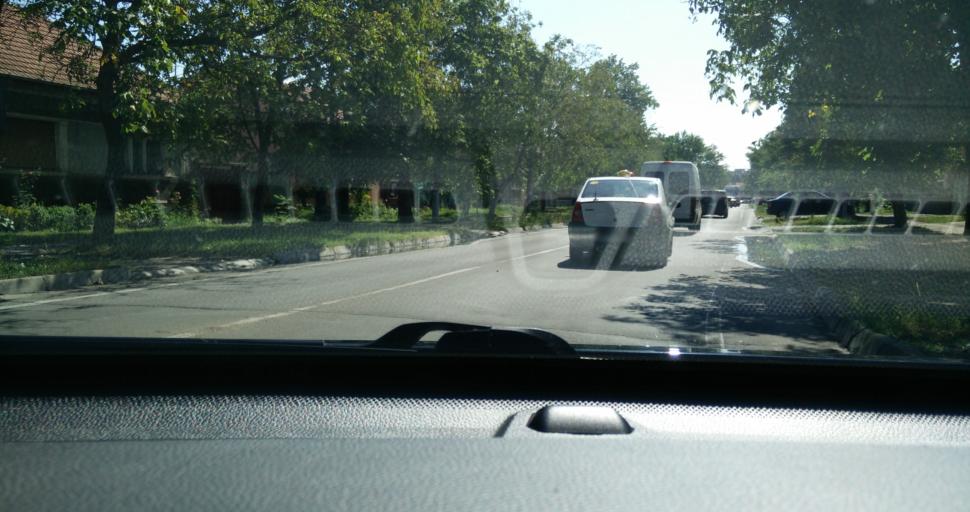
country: RO
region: Bihor
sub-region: Comuna Biharea
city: Oradea
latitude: 47.0430
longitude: 21.9356
